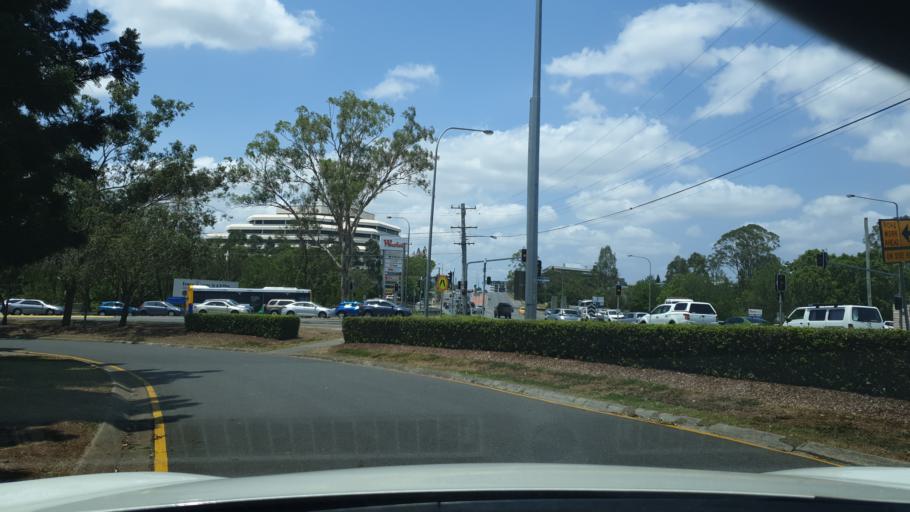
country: AU
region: Queensland
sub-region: Brisbane
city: Chermside West
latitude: -27.3785
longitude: 153.0294
